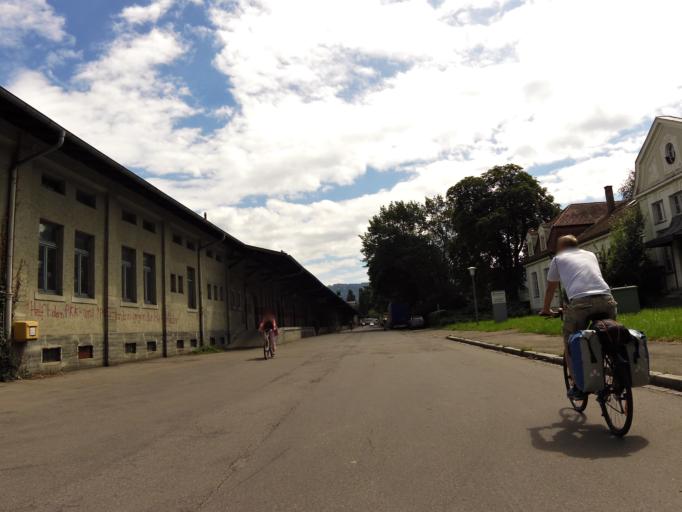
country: DE
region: Bavaria
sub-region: Swabia
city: Lindau
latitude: 47.5512
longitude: 9.7033
